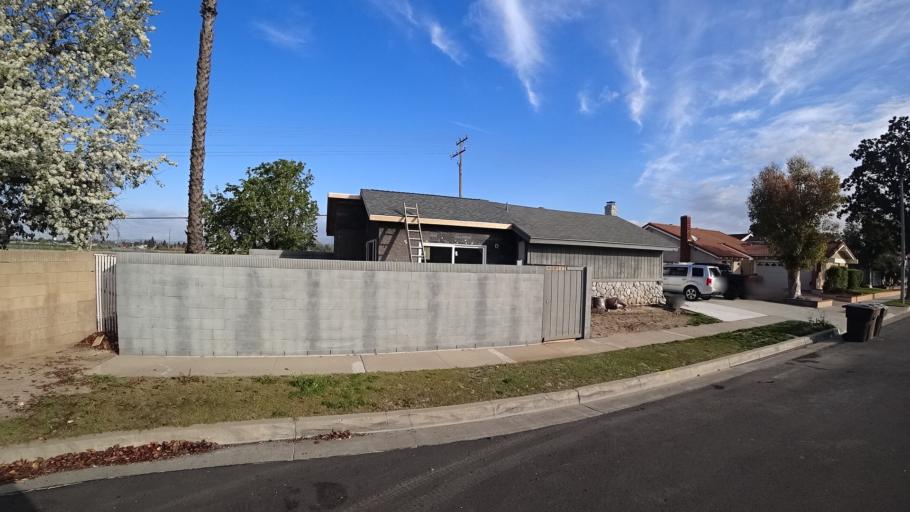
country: US
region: California
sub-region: Orange County
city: Yorba Linda
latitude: 33.8549
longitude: -117.8148
